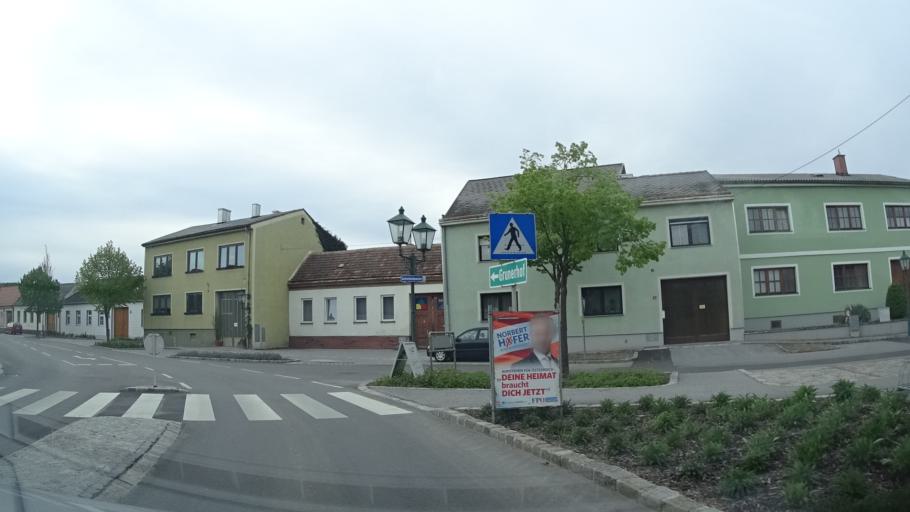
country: AT
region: Lower Austria
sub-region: Politischer Bezirk Korneuburg
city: Leobendorf
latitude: 48.3776
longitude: 16.3269
